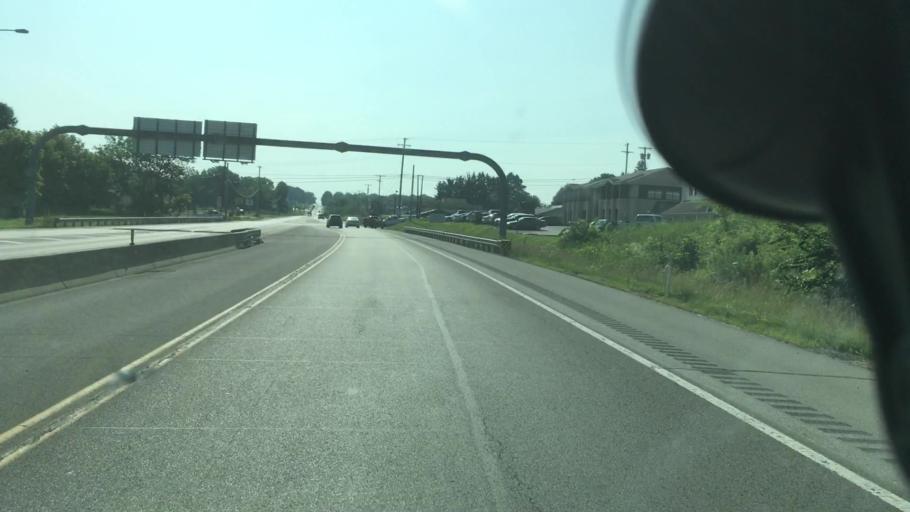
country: US
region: Pennsylvania
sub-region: Lawrence County
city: New Castle
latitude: 40.9772
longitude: -80.2965
